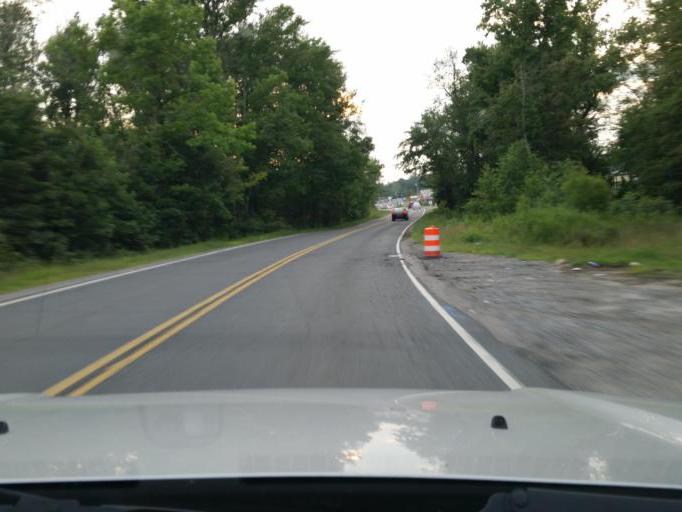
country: US
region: Virginia
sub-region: Spotsylvania County
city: Spotsylvania Courthouse
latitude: 38.1324
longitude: -77.5167
